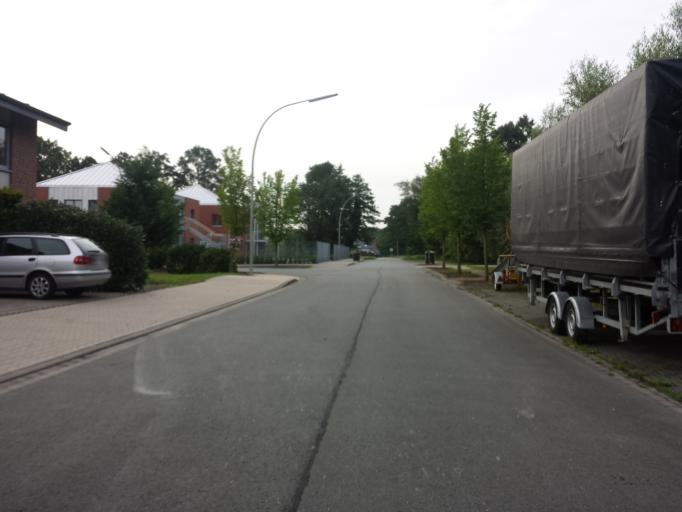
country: DE
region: North Rhine-Westphalia
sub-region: Regierungsbezirk Detmold
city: Harsewinkel
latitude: 51.9693
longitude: 8.2465
